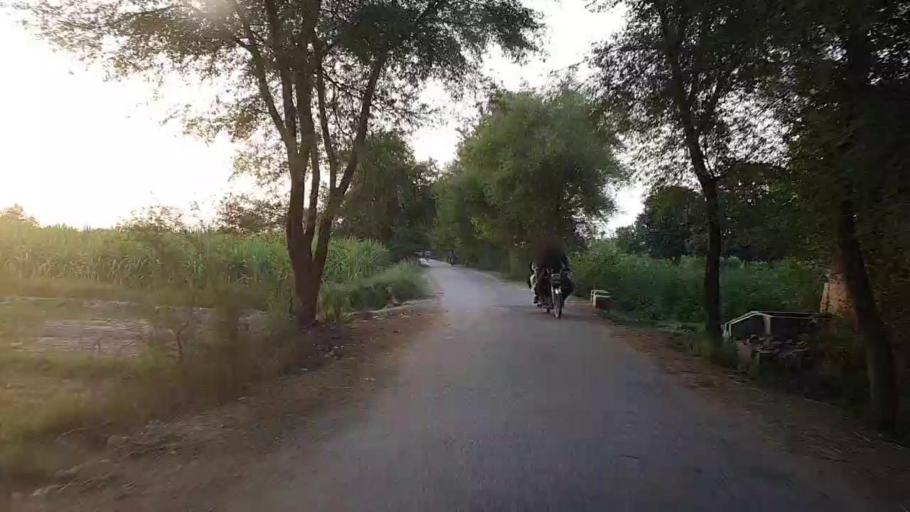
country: PK
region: Sindh
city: Ubauro
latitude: 28.2990
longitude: 69.7981
